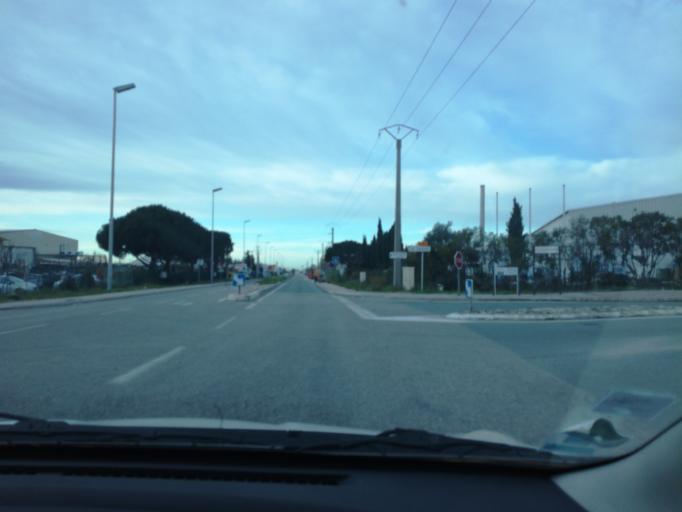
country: FR
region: Provence-Alpes-Cote d'Azur
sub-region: Departement du Var
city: La Farlede
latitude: 43.1540
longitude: 6.0451
